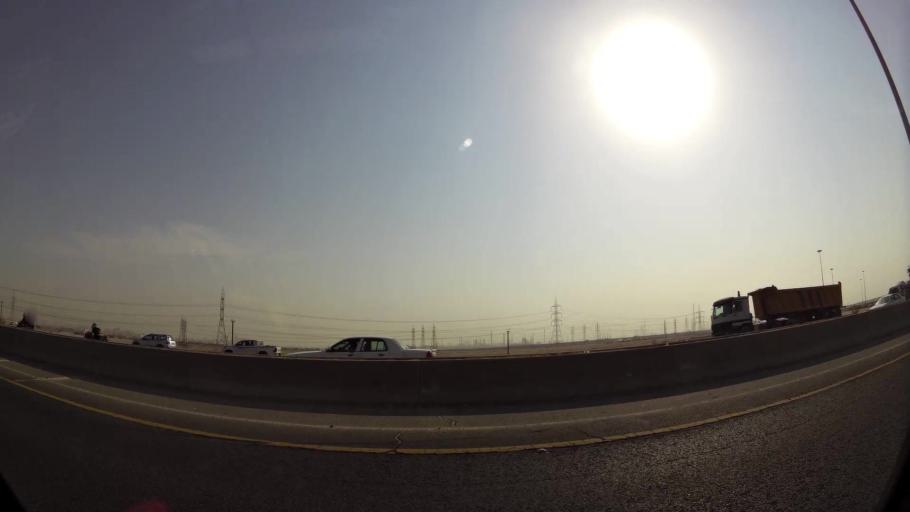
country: KW
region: Al Ahmadi
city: Al Ahmadi
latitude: 29.0666
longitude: 48.0988
